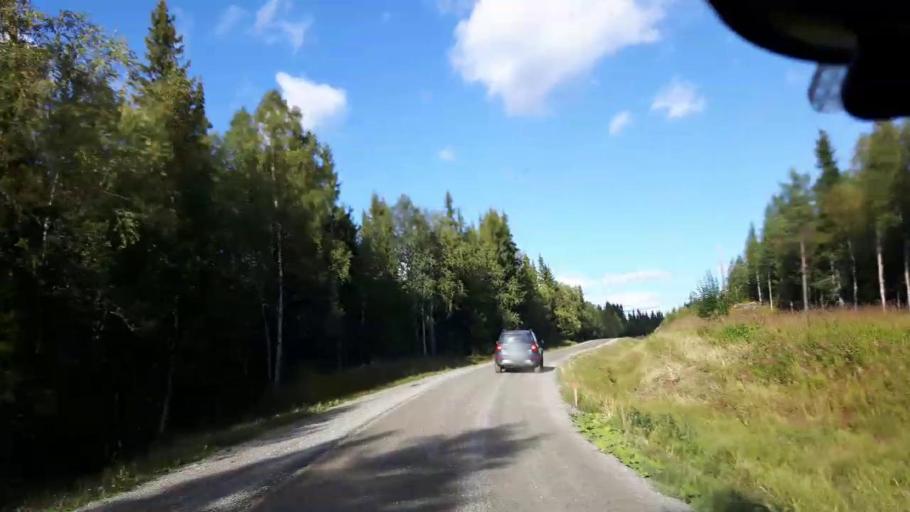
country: SE
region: Jaemtland
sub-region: Ragunda Kommun
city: Hammarstrand
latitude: 63.4154
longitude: 16.1022
